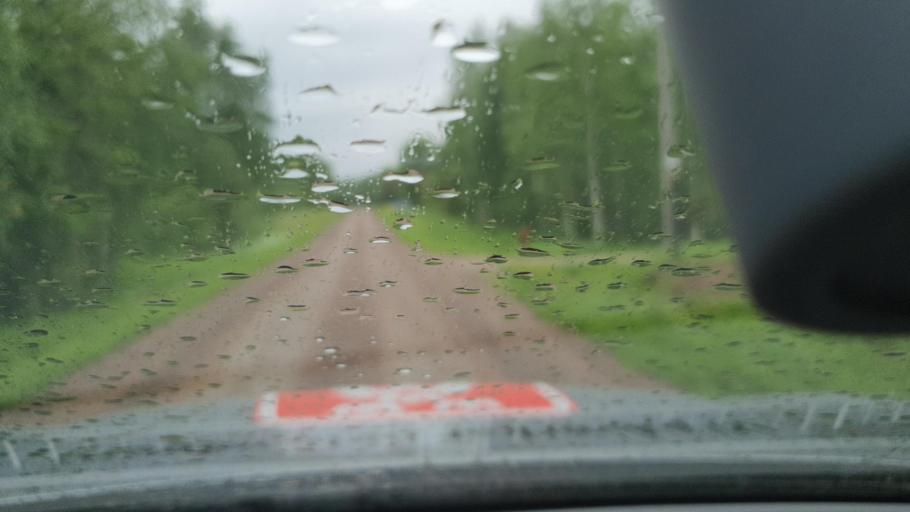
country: SE
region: Norrbotten
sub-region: Overkalix Kommun
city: OEverkalix
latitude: 66.5487
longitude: 22.7452
